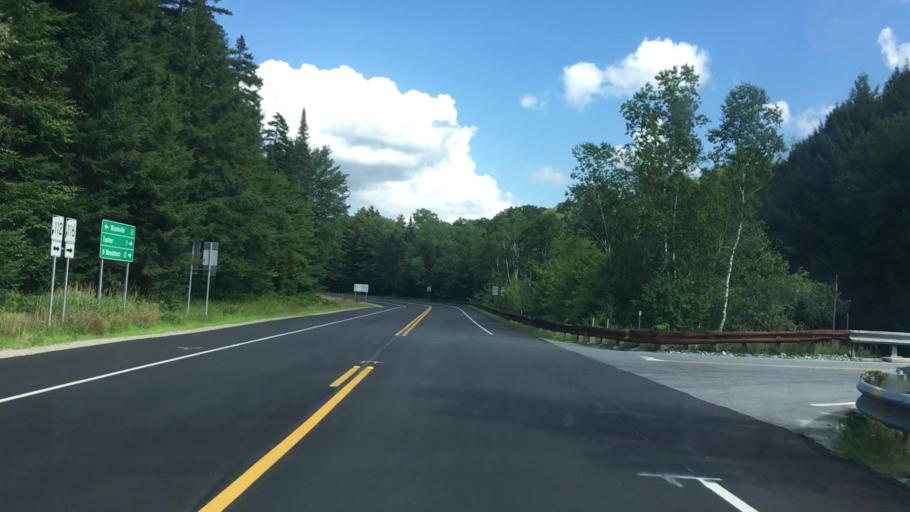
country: US
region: New Hampshire
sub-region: Grafton County
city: North Haverhill
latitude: 44.0982
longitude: -71.8485
